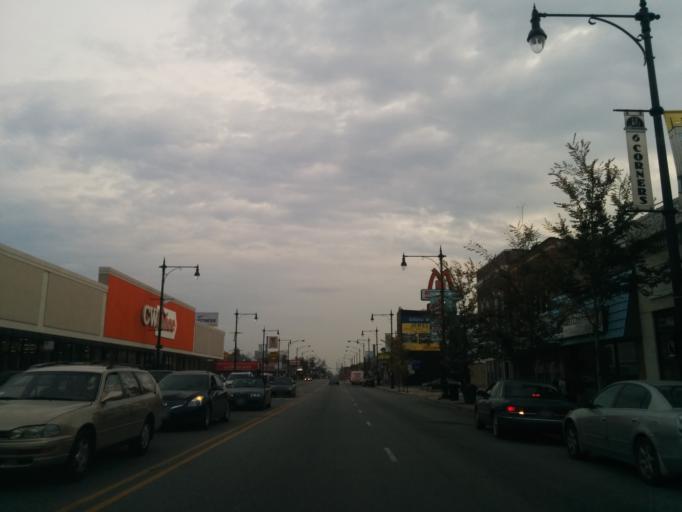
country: US
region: Illinois
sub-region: Cook County
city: Lincolnwood
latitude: 41.9533
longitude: -87.7476
